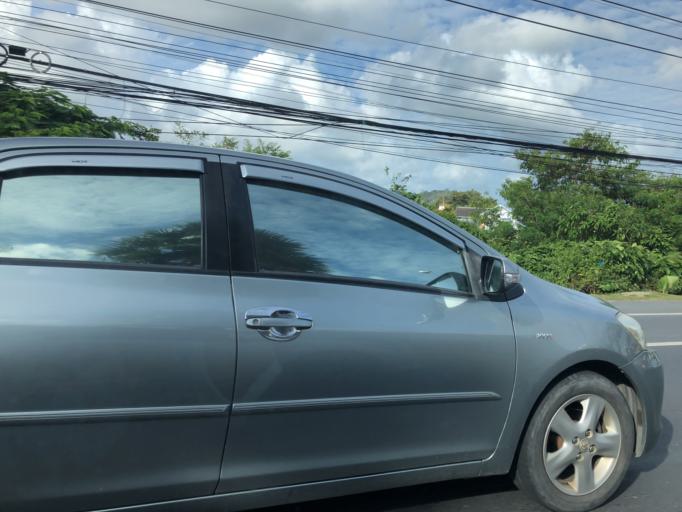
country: TH
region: Phuket
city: Thalang
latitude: 8.0028
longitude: 98.3460
